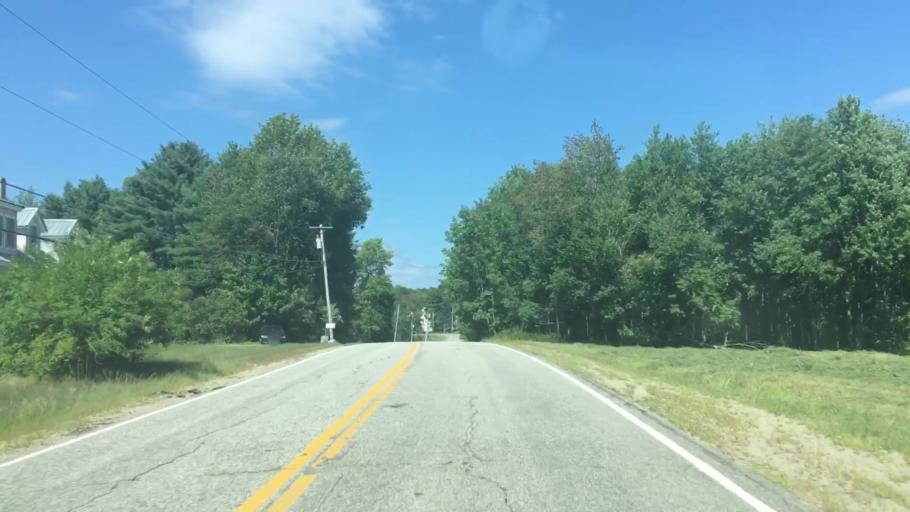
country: US
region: Maine
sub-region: Kennebec County
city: Monmouth
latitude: 44.1865
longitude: -69.9389
